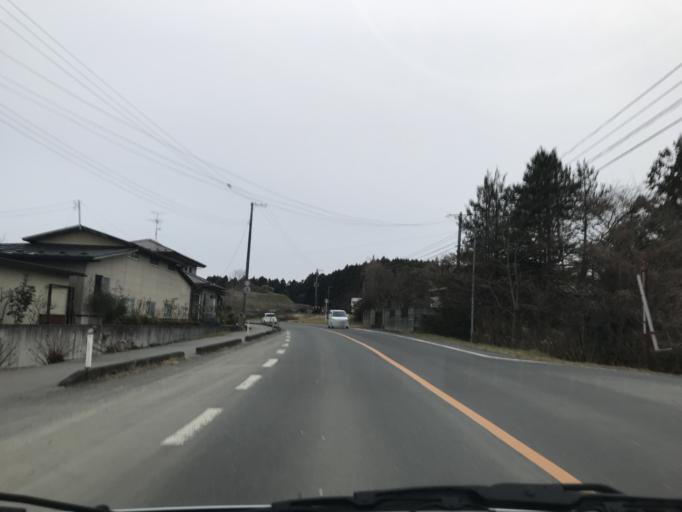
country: JP
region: Miyagi
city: Wakuya
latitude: 38.6861
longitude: 141.1315
